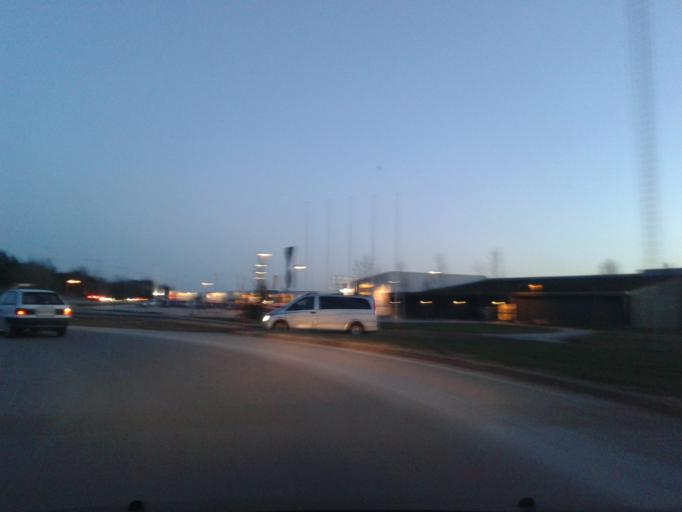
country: SE
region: Gotland
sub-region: Gotland
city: Visby
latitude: 57.6250
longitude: 18.3210
